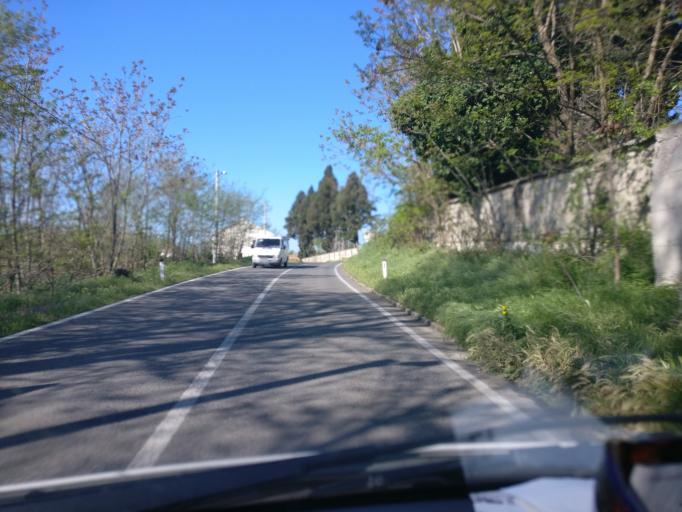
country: BA
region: Federation of Bosnia and Herzegovina
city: Tasovcici
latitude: 43.1362
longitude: 17.7773
